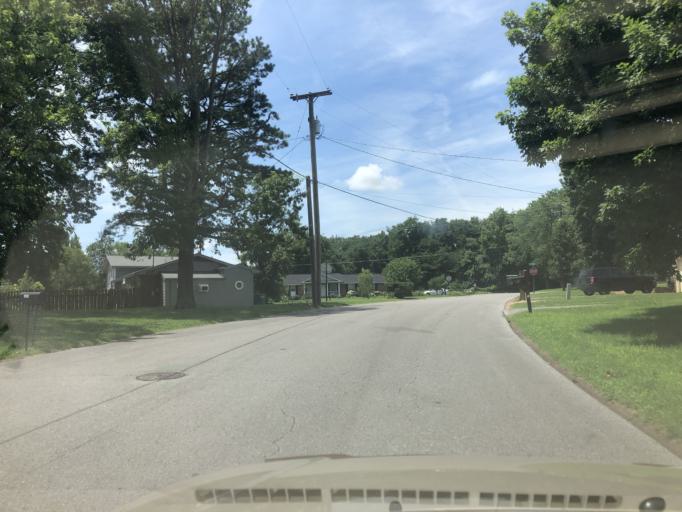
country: US
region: Tennessee
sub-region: Davidson County
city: Lakewood
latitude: 36.2477
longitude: -86.6726
